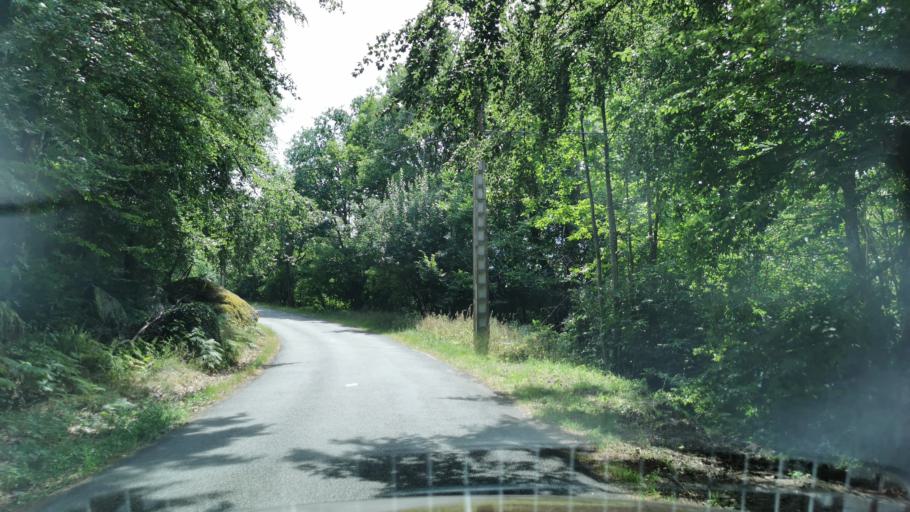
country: FR
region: Bourgogne
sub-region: Departement de Saone-et-Loire
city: Etang-sur-Arroux
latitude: 46.8115
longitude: 4.2554
